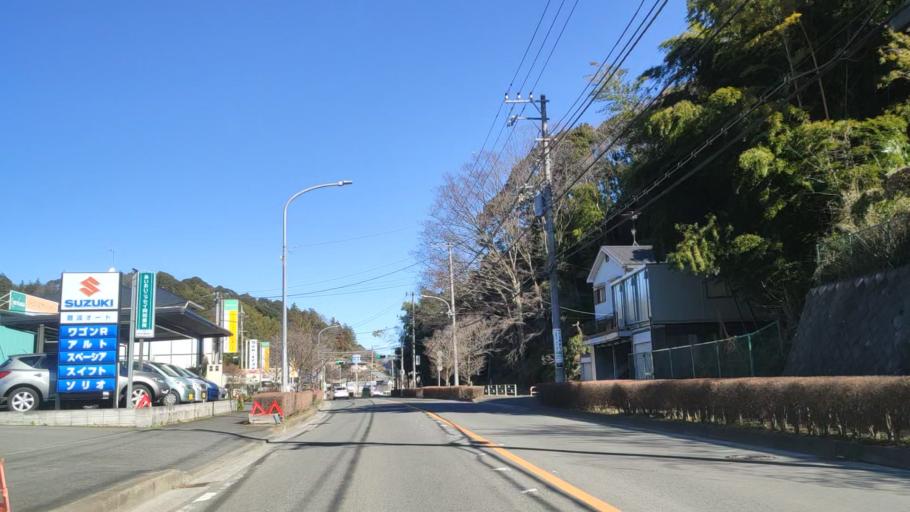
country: JP
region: Kanagawa
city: Minami-rinkan
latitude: 35.5049
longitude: 139.5161
